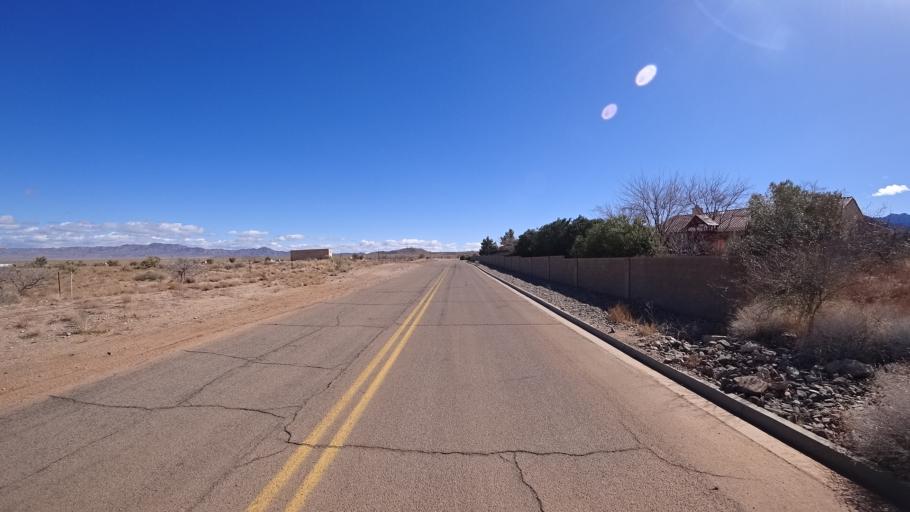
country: US
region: Arizona
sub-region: Mohave County
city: Kingman
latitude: 35.2040
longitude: -113.9610
